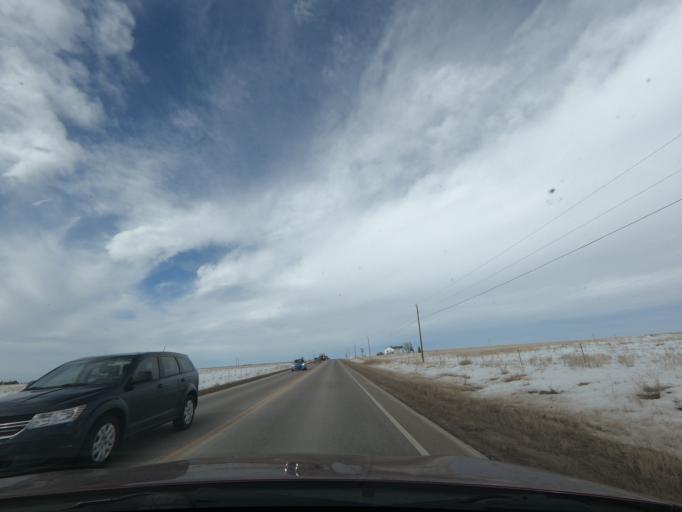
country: US
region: Colorado
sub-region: Elbert County
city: Ponderosa Park
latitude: 39.3376
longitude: -104.7340
